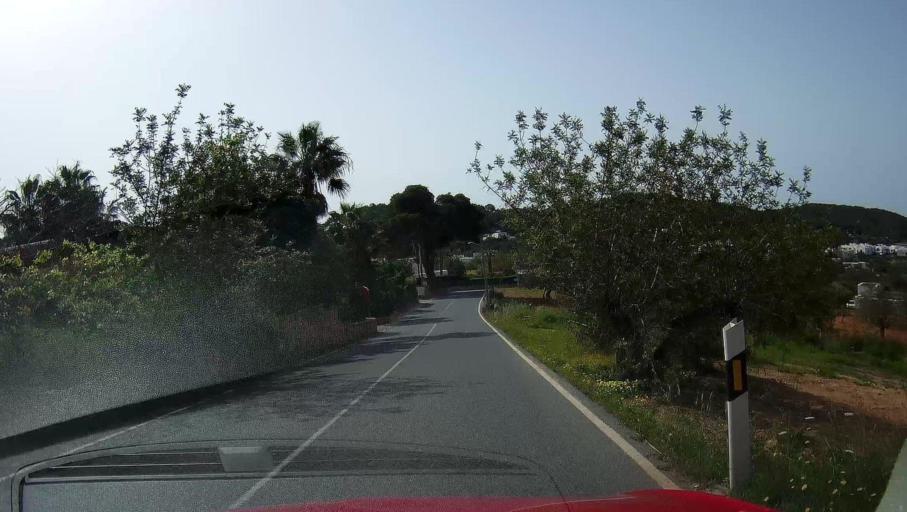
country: ES
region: Balearic Islands
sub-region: Illes Balears
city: Santa Eularia des Riu
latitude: 39.0379
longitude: 1.5657
